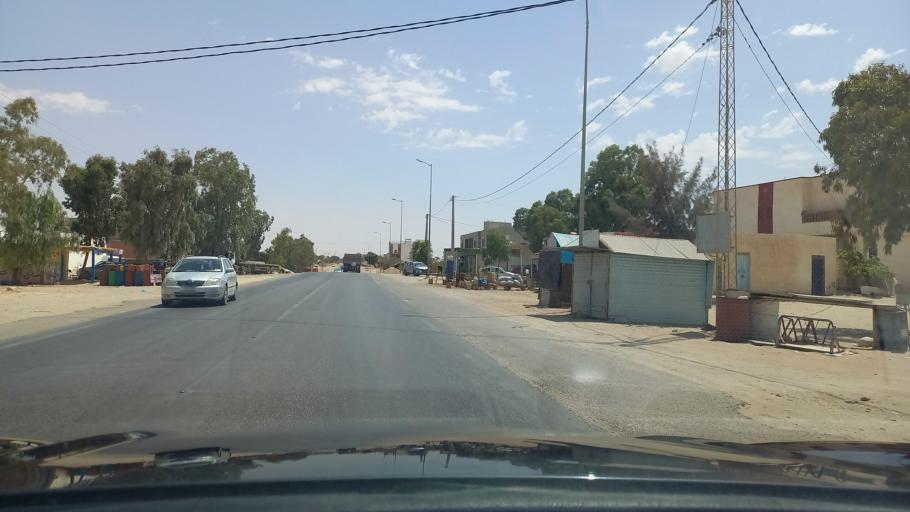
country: TN
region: Madanin
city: Medenine
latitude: 33.3767
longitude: 10.4440
